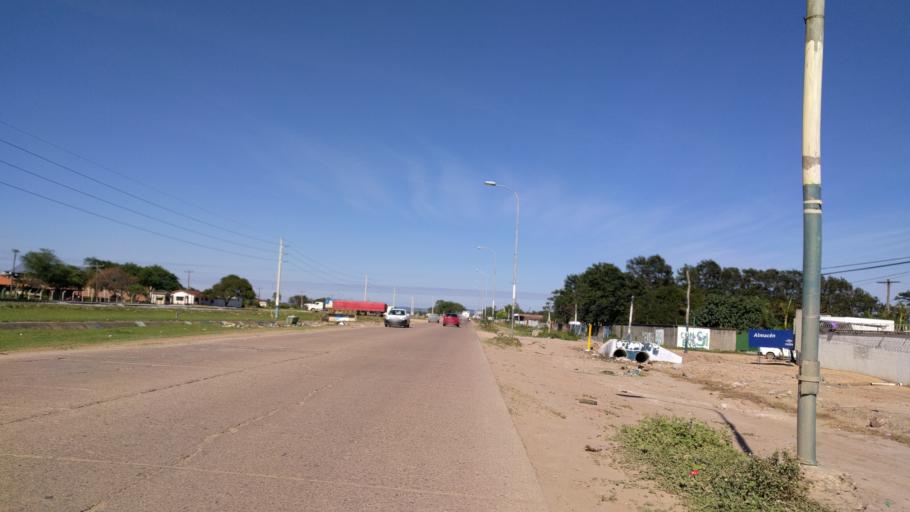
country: BO
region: Santa Cruz
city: Santa Cruz de la Sierra
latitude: -17.8689
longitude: -63.1910
